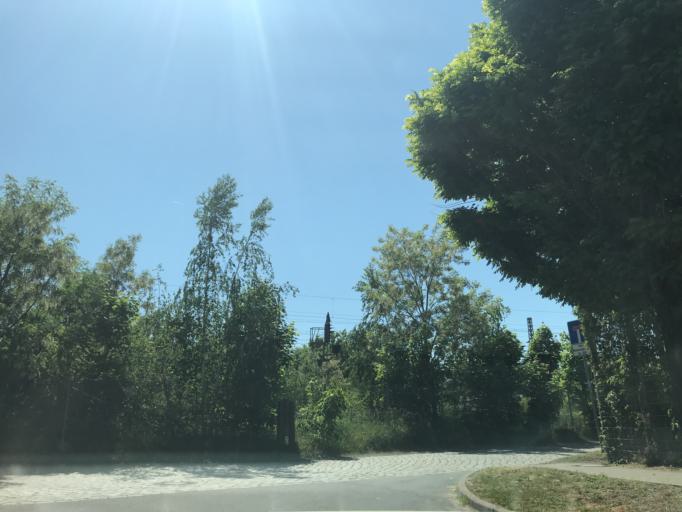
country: DE
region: Brandenburg
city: Falkensee
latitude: 52.5589
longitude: 13.0948
